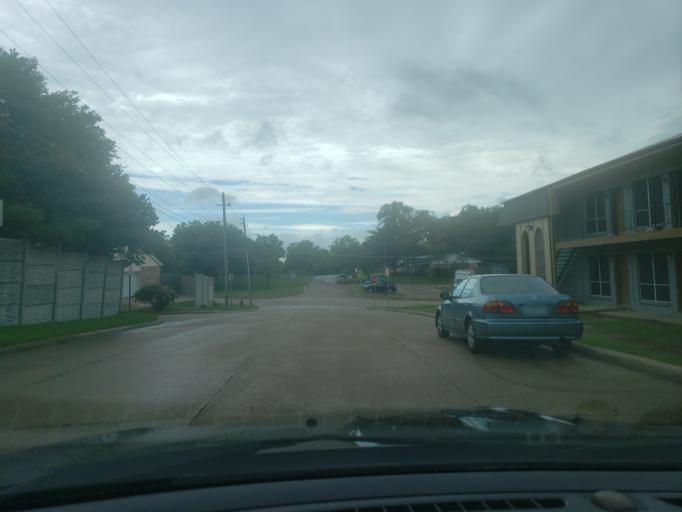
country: US
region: Texas
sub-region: Dallas County
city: Grand Prairie
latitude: 32.7489
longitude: -97.0000
